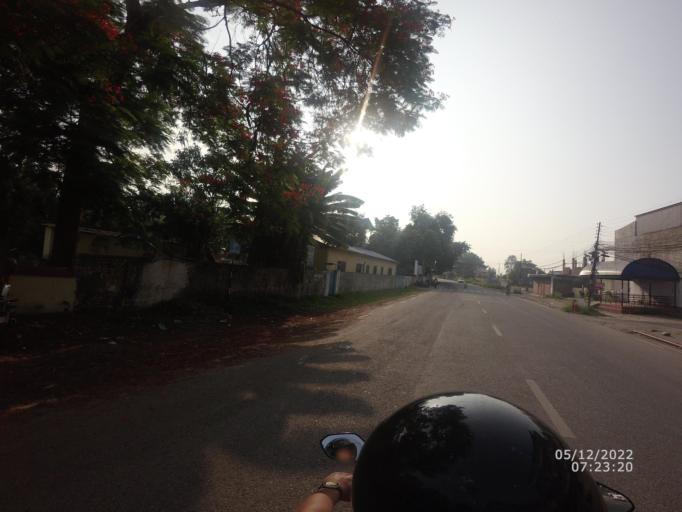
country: NP
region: Central Region
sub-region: Narayani Zone
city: Bharatpur
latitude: 27.6807
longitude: 84.4344
